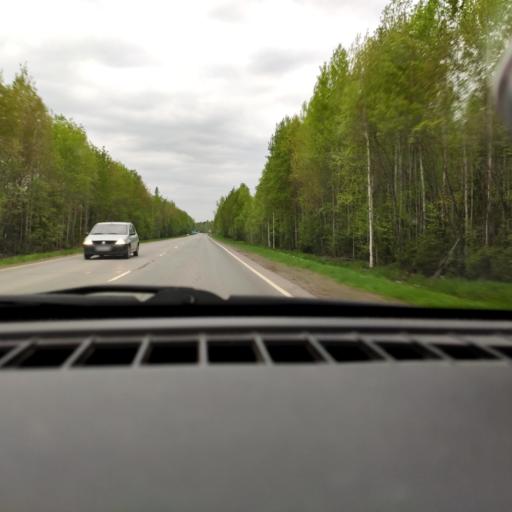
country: RU
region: Perm
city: Polazna
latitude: 58.2856
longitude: 56.1640
